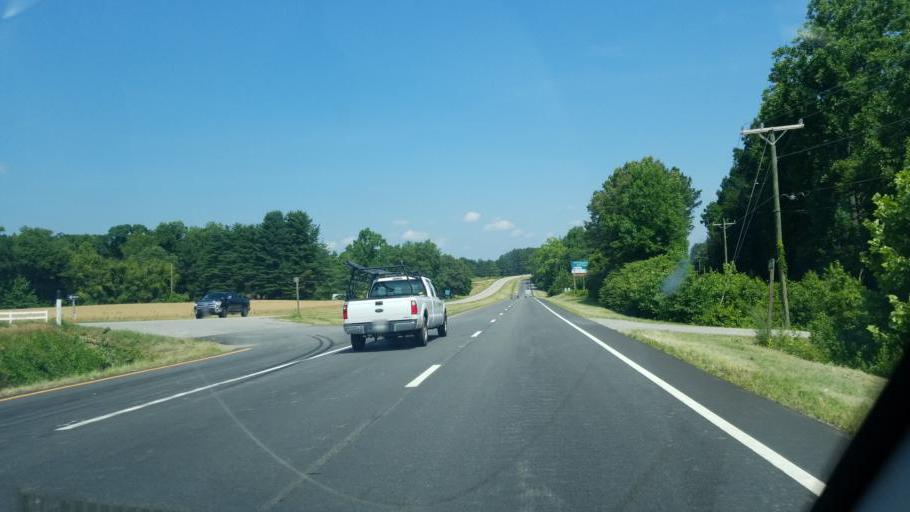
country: US
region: Virginia
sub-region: Pittsylvania County
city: Chatham
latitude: 36.7515
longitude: -79.3835
